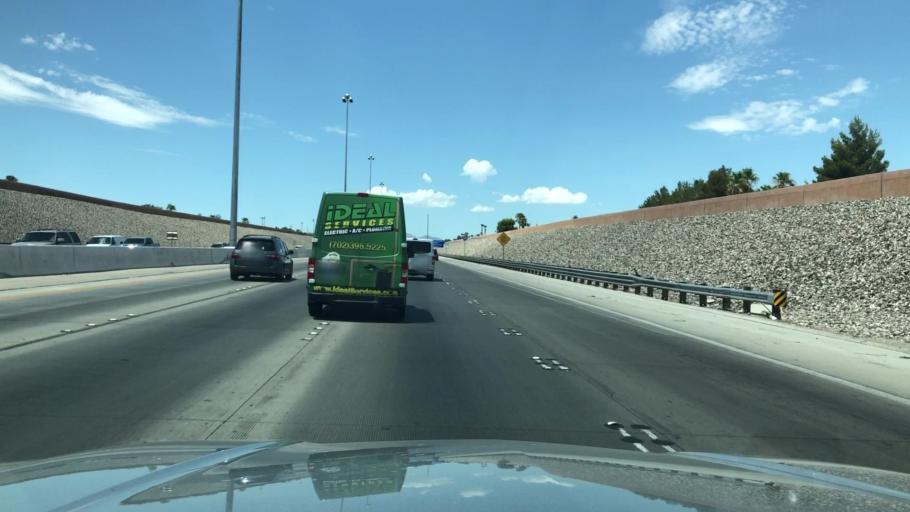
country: US
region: Nevada
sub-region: Clark County
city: Whitney
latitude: 36.0269
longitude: -115.0680
